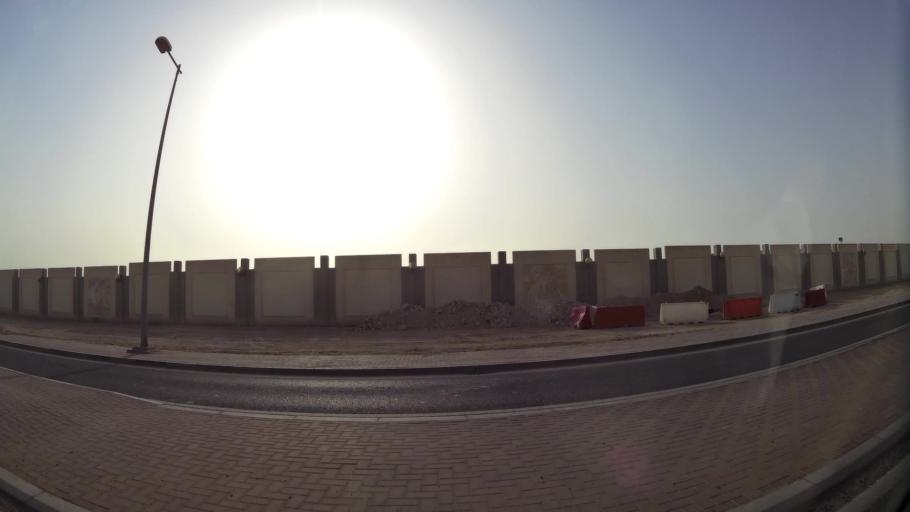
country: QA
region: Baladiyat ar Rayyan
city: Ar Rayyan
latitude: 25.2455
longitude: 51.4379
